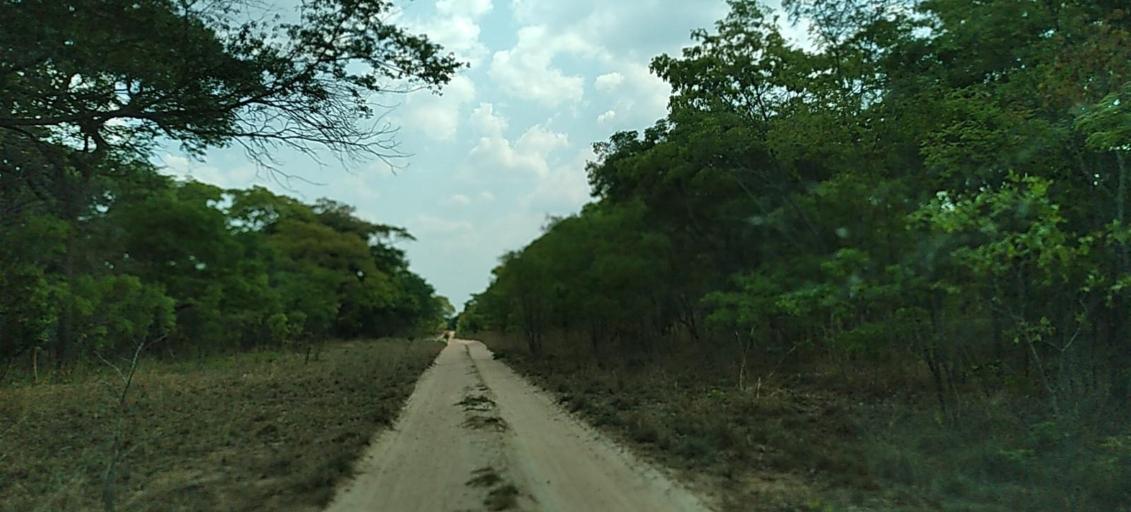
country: ZM
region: Copperbelt
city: Mpongwe
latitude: -13.8510
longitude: 27.9314
